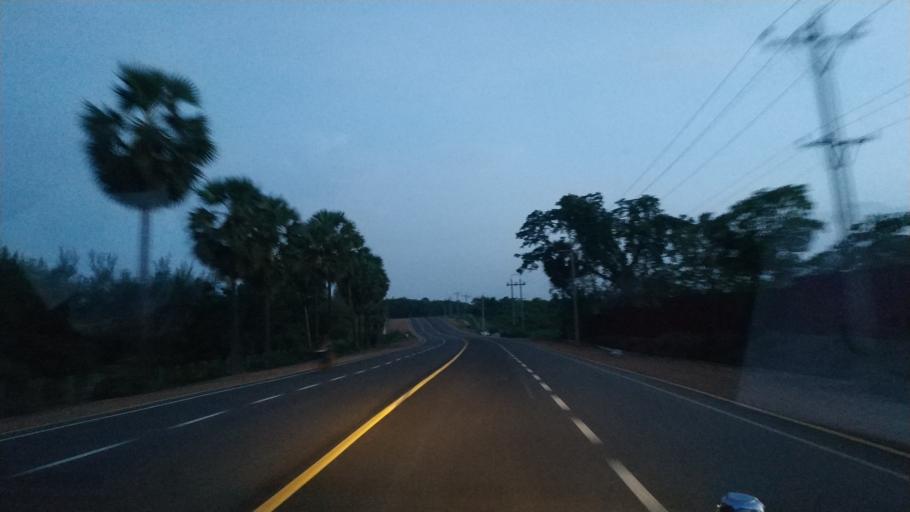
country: MM
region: Mon
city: Kyaikto
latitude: 17.3792
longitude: 97.0534
